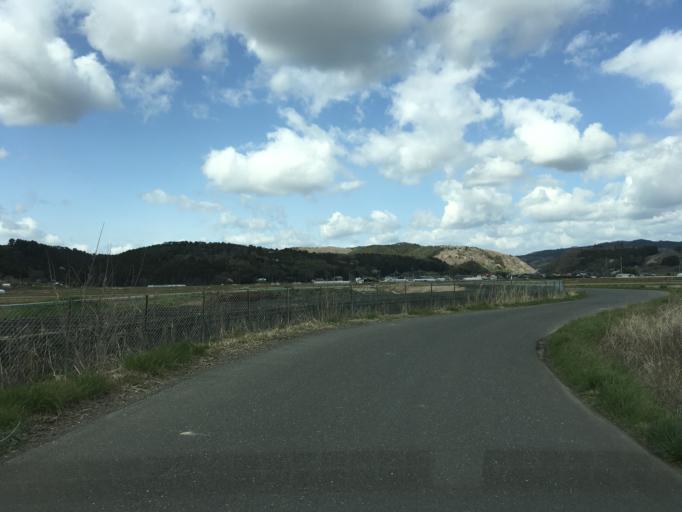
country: JP
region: Iwate
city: Ichinoseki
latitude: 38.7545
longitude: 141.2640
